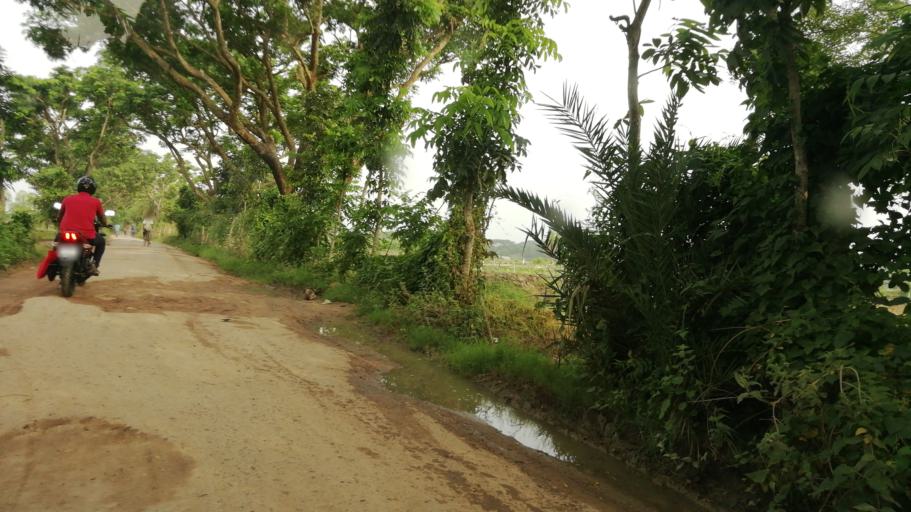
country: BD
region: Khulna
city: Bhatpara Abhaynagar
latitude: 23.0399
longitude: 89.3237
